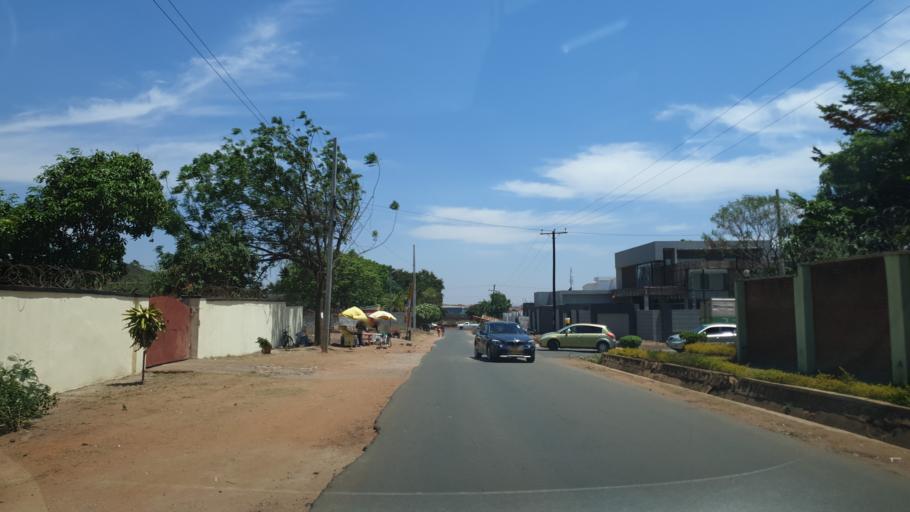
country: MW
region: Central Region
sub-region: Lilongwe District
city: Lilongwe
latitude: -13.9762
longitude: 33.7457
